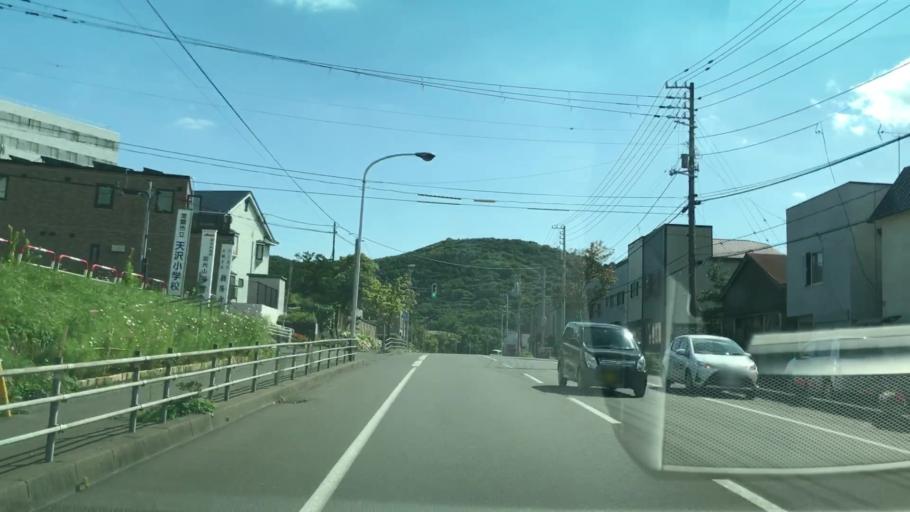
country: JP
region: Hokkaido
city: Muroran
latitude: 42.3227
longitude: 140.9968
